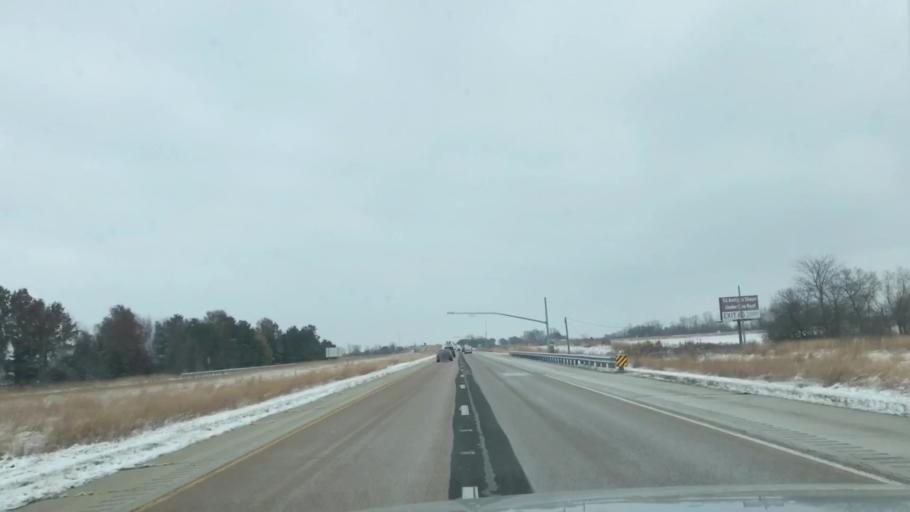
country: US
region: Illinois
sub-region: Montgomery County
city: Litchfield
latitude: 39.2053
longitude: -89.6589
